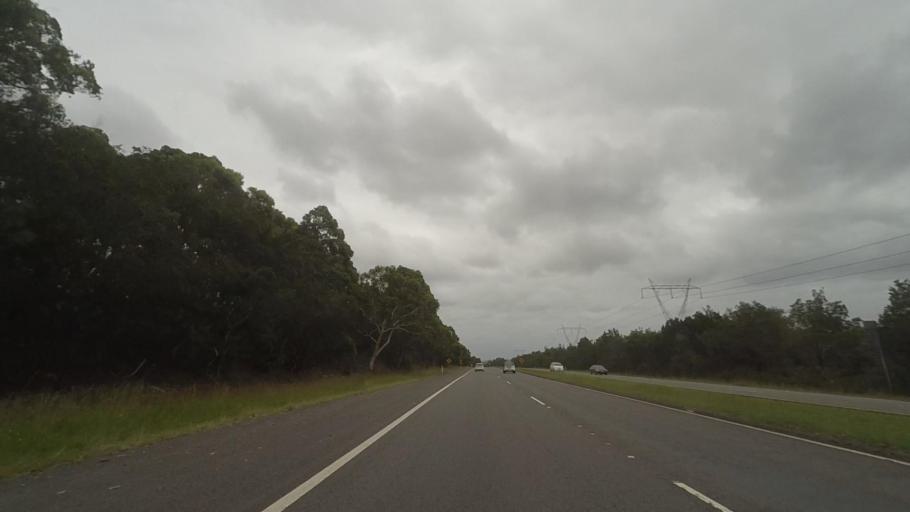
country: AU
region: New South Wales
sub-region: Wyong Shire
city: Charmhaven
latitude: -33.2060
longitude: 151.5128
